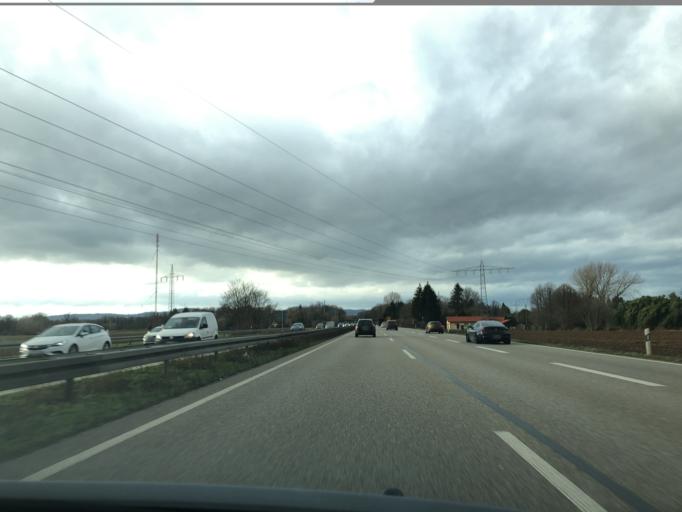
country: DE
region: Baden-Wuerttemberg
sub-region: Freiburg Region
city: Umkirch
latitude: 48.0103
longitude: 7.7998
